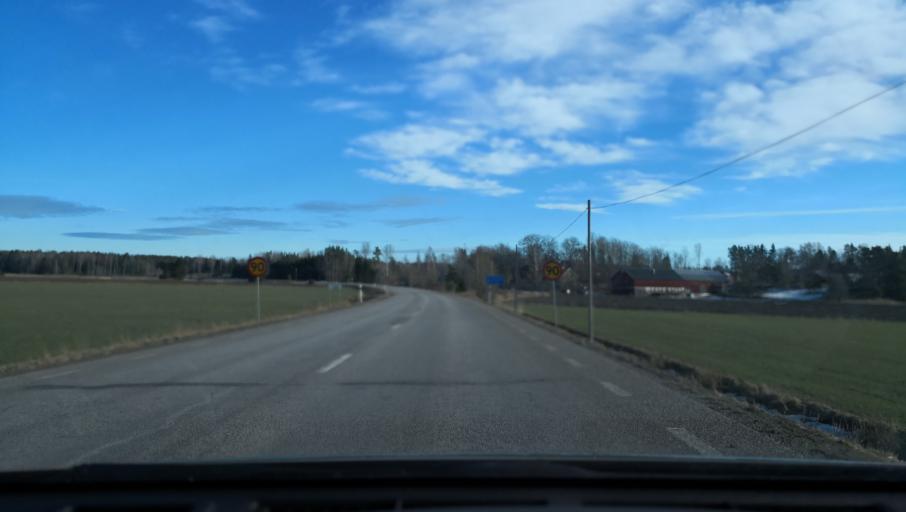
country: SE
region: Uppsala
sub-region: Osthammars Kommun
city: Osterbybruk
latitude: 60.1638
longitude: 17.9804
